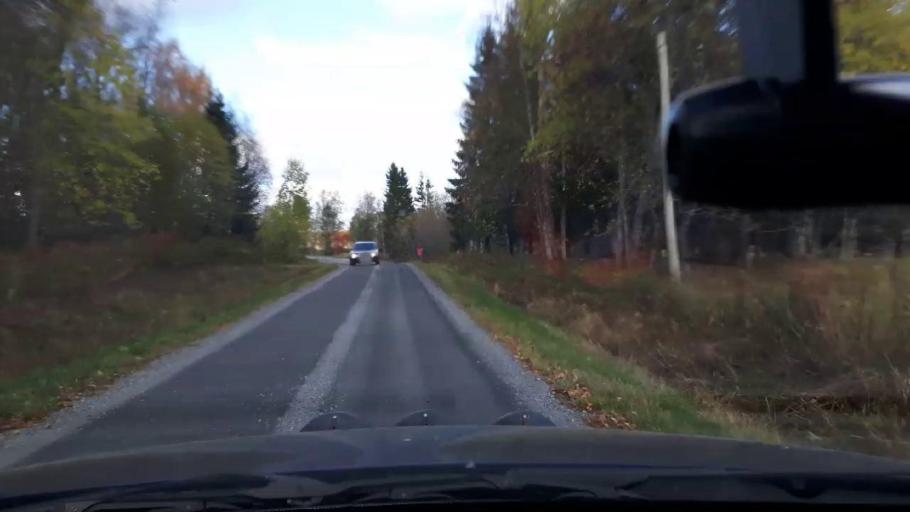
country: SE
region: Jaemtland
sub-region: Bergs Kommun
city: Hoverberg
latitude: 63.0550
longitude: 14.2390
